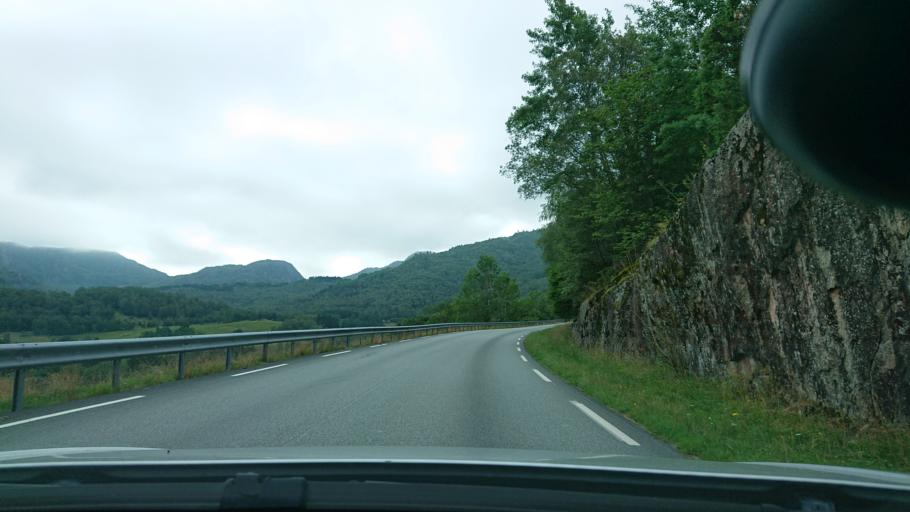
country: NO
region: Rogaland
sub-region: Hjelmeland
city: Hjelmelandsvagen
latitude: 59.2247
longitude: 6.2109
